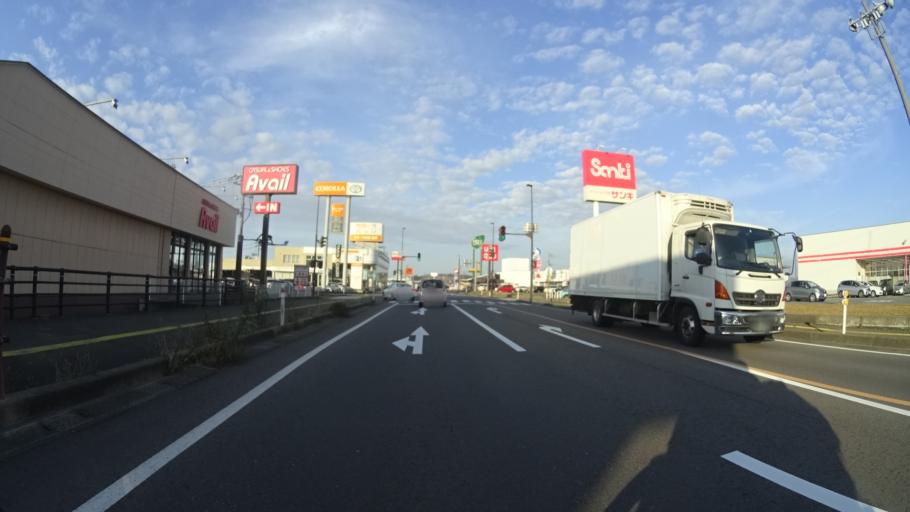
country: JP
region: Niigata
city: Kashiwazaki
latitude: 37.3774
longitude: 138.5801
